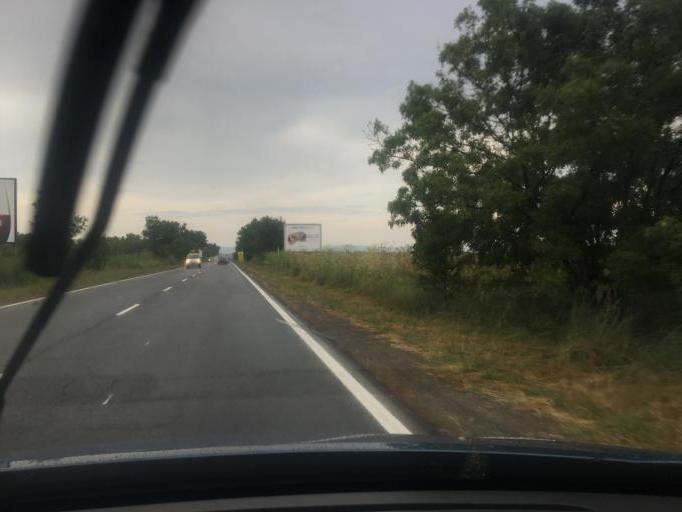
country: BG
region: Burgas
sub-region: Obshtina Pomorie
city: Pomorie
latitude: 42.5908
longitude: 27.6123
